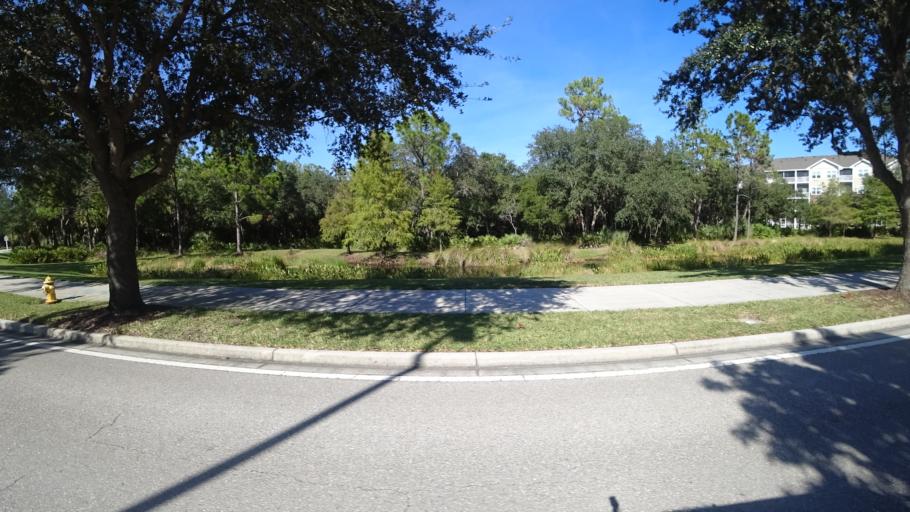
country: US
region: Florida
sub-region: Sarasota County
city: The Meadows
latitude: 27.3915
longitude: -82.4443
